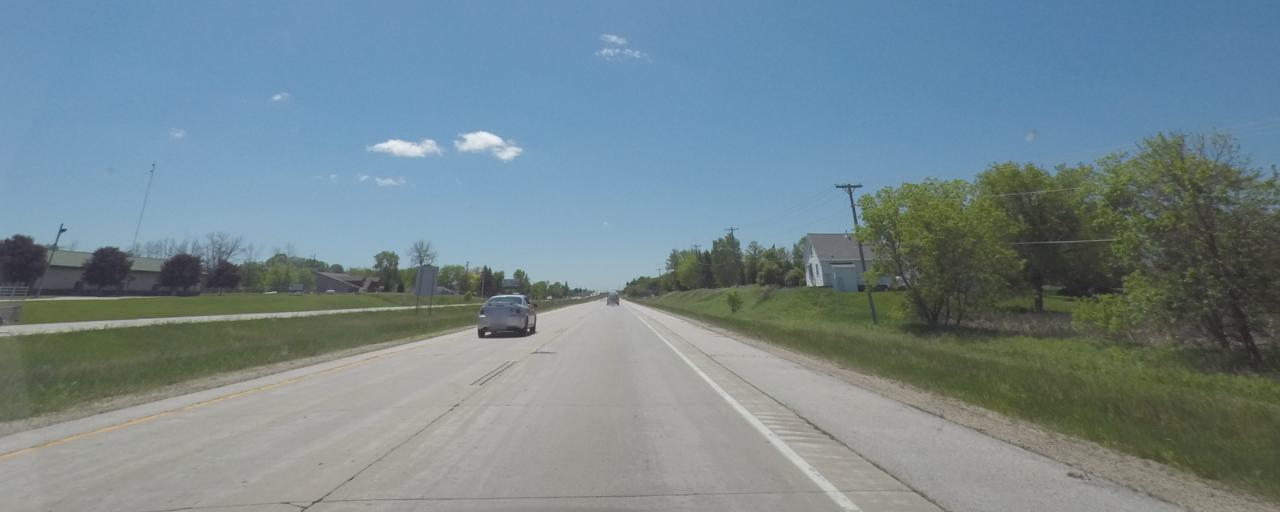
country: US
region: Wisconsin
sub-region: Sheboygan County
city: Plymouth
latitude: 43.7450
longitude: -87.9414
